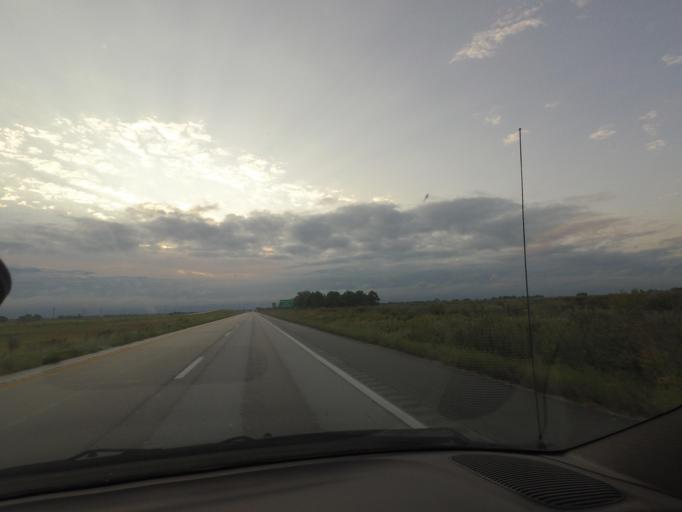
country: US
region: Missouri
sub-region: Shelby County
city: Shelbina
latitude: 39.7062
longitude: -92.0935
